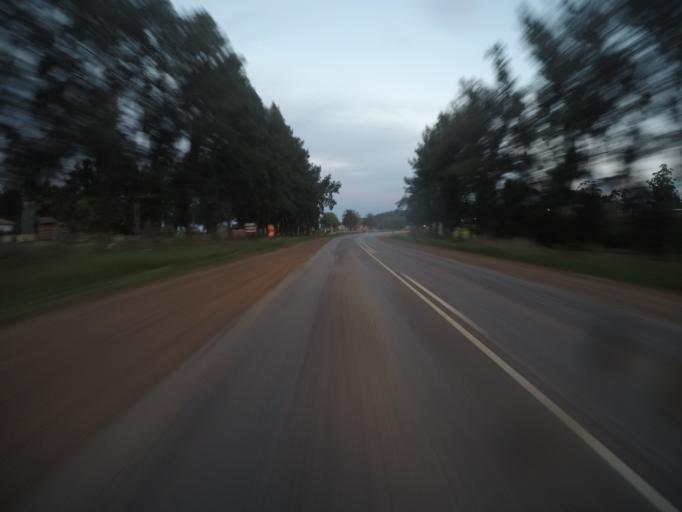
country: ZA
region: Western Cape
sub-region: Eden District Municipality
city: Plettenberg Bay
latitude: -33.8022
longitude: 23.6648
